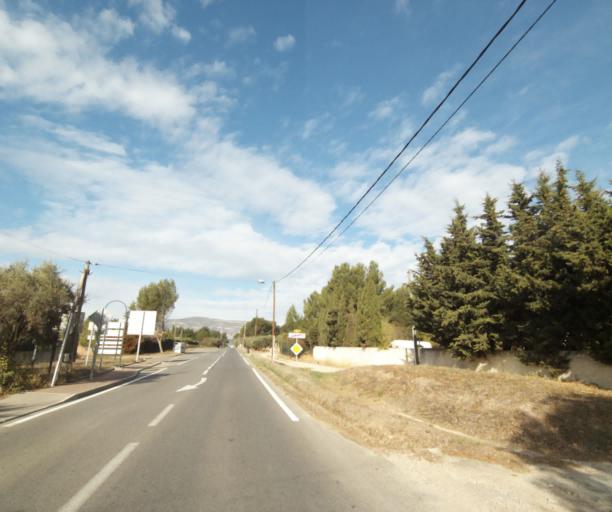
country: FR
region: Provence-Alpes-Cote d'Azur
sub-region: Departement des Bouches-du-Rhone
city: Gemenos
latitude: 43.3033
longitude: 5.6155
